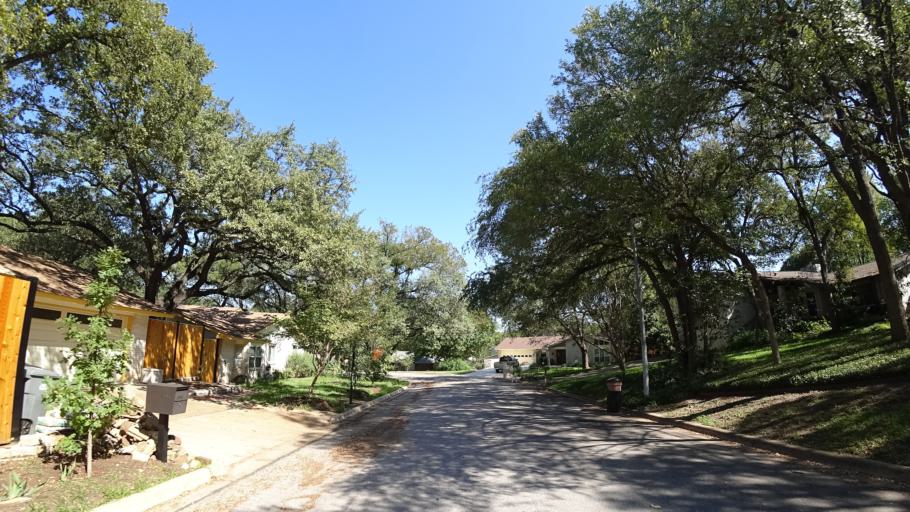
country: US
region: Texas
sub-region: Travis County
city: Rollingwood
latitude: 30.2517
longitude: -97.7902
